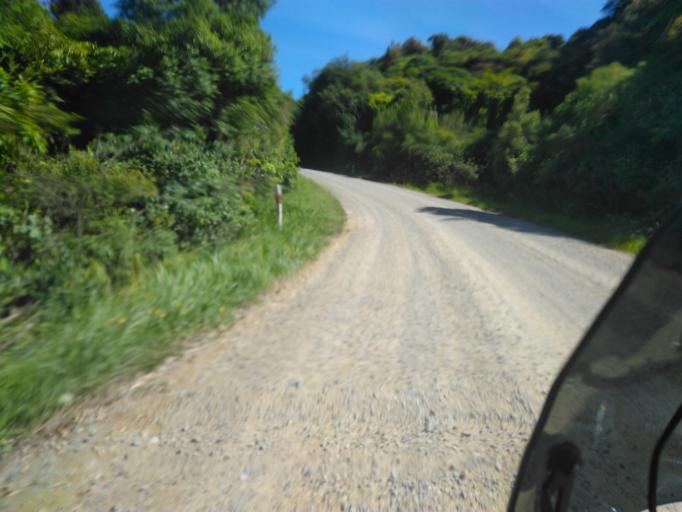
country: NZ
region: Hawke's Bay
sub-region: Wairoa District
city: Wairoa
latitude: -38.7944
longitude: 177.1250
